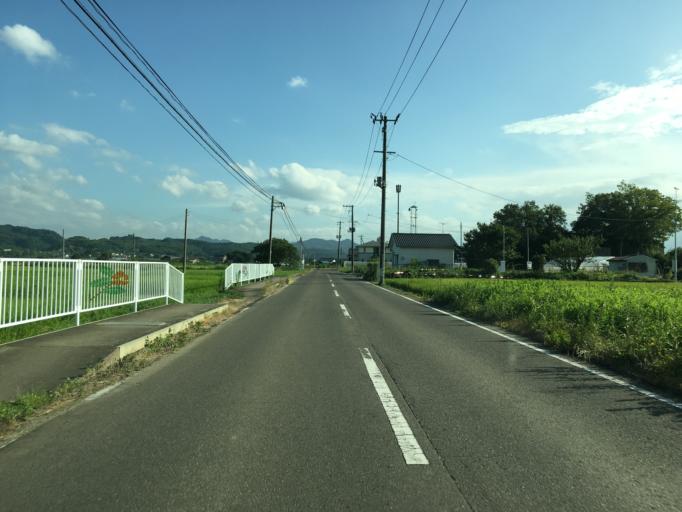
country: JP
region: Fukushima
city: Yanagawamachi-saiwaicho
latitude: 37.8318
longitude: 140.5833
